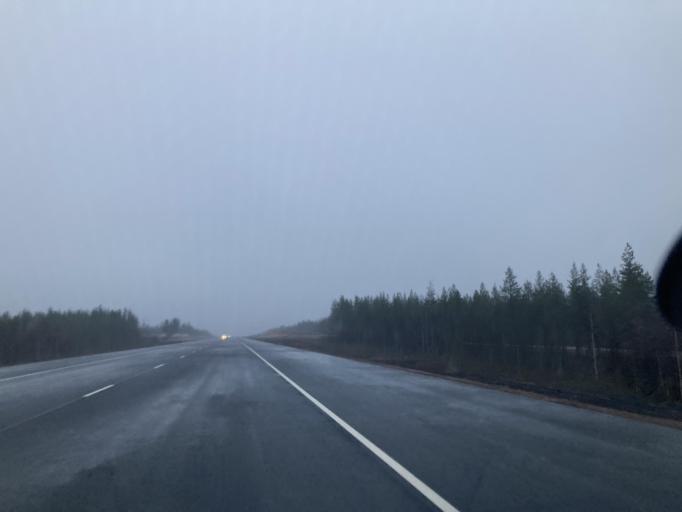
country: FI
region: Lapland
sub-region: Rovaniemi
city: Rovaniemi
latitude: 66.5834
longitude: 25.8007
